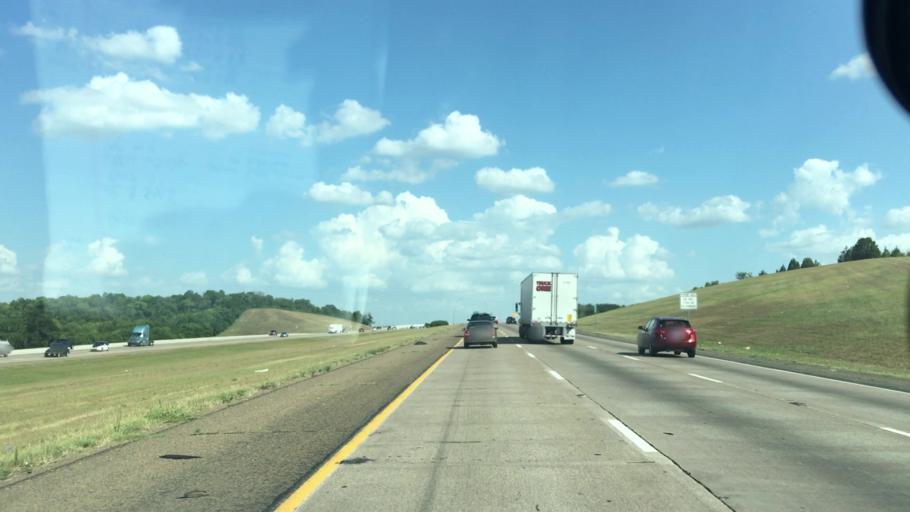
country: US
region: Texas
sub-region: Dallas County
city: Hutchins
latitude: 32.6714
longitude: -96.7356
